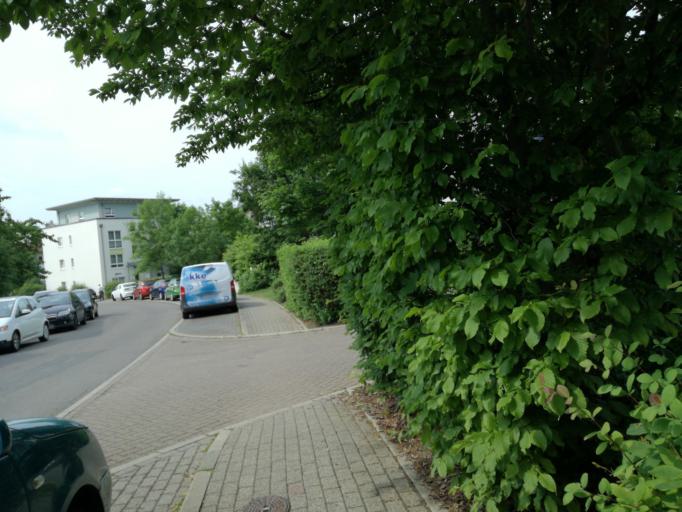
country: DE
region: Saxony
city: Leipzig
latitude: 51.3811
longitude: 12.3286
